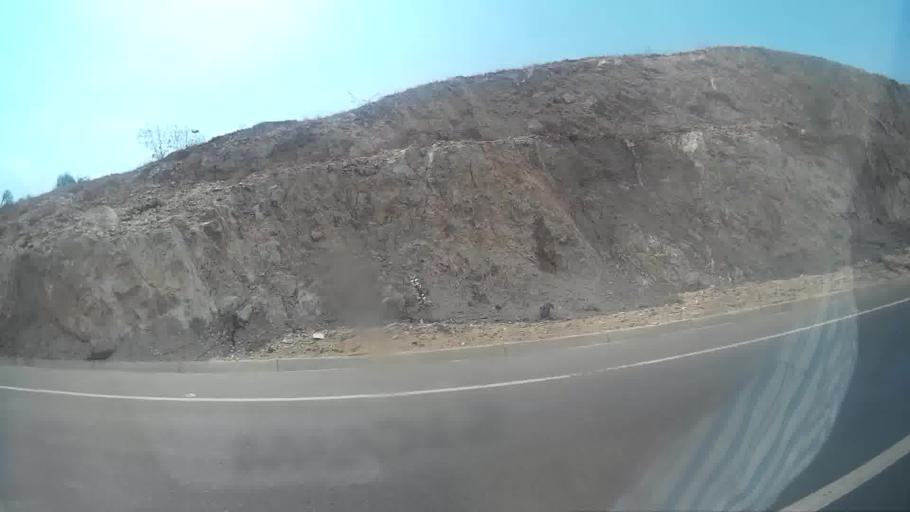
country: CO
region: Magdalena
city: Santa Marta
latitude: 11.1844
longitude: -74.2231
